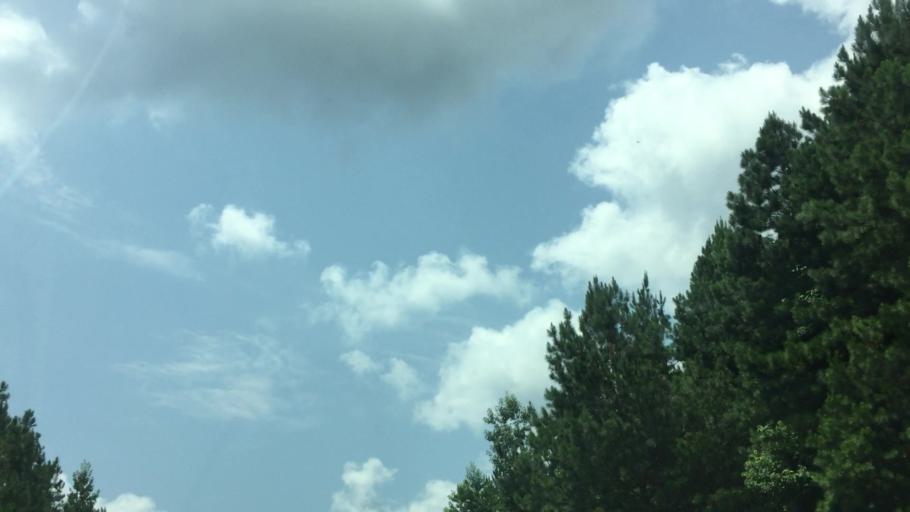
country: US
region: Georgia
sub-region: Fulton County
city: Chattahoochee Hills
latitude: 33.5675
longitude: -84.7362
